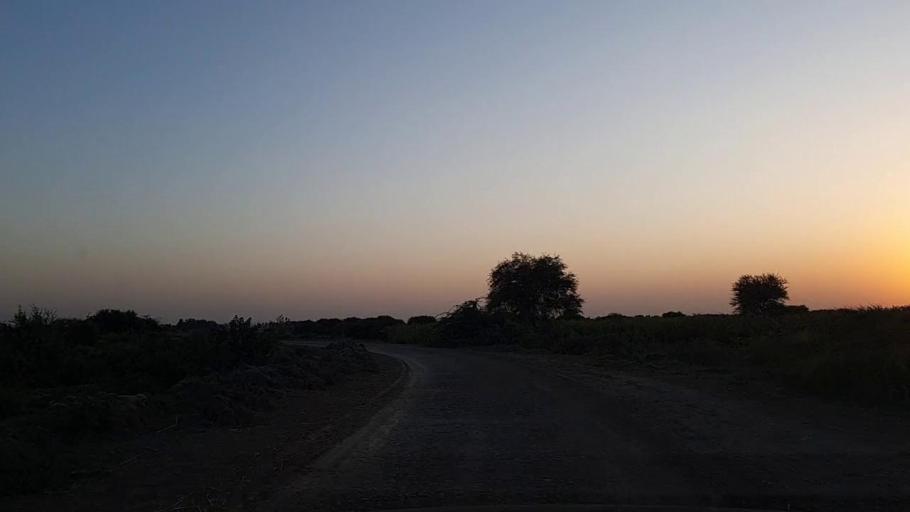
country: PK
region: Sindh
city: Mirpur Batoro
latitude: 24.6240
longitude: 68.1844
